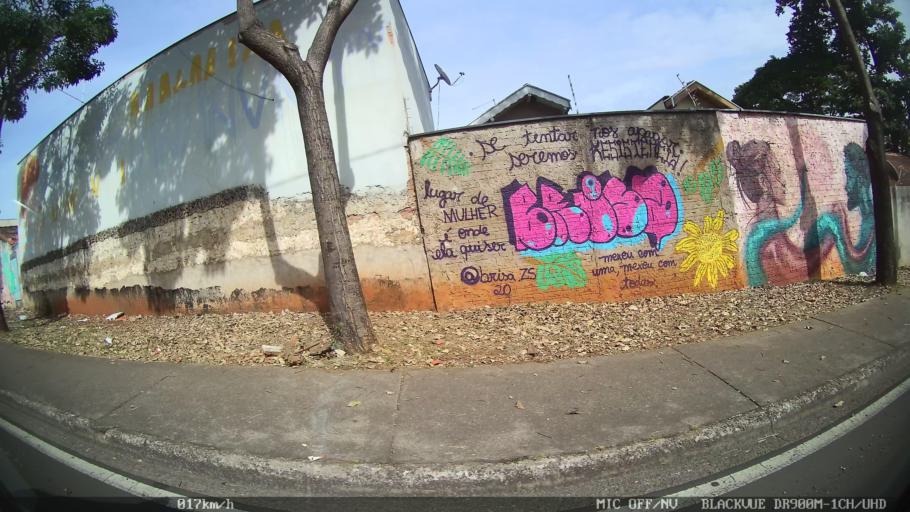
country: BR
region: Sao Paulo
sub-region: Piracicaba
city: Piracicaba
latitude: -22.7413
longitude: -47.6446
